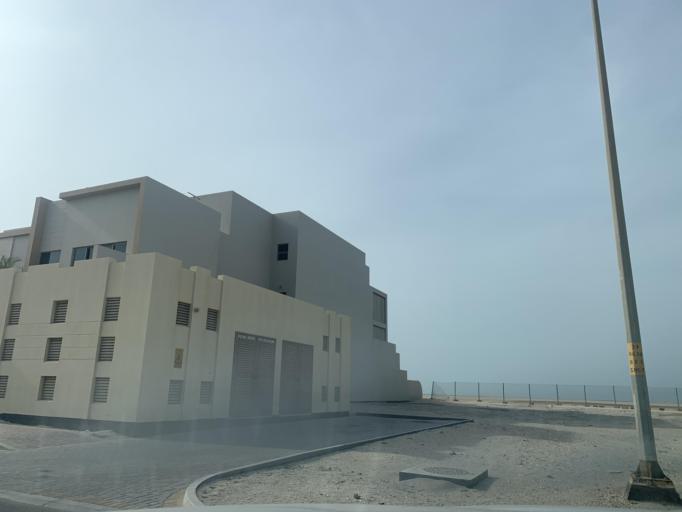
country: BH
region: Muharraq
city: Al Muharraq
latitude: 26.3233
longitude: 50.6288
